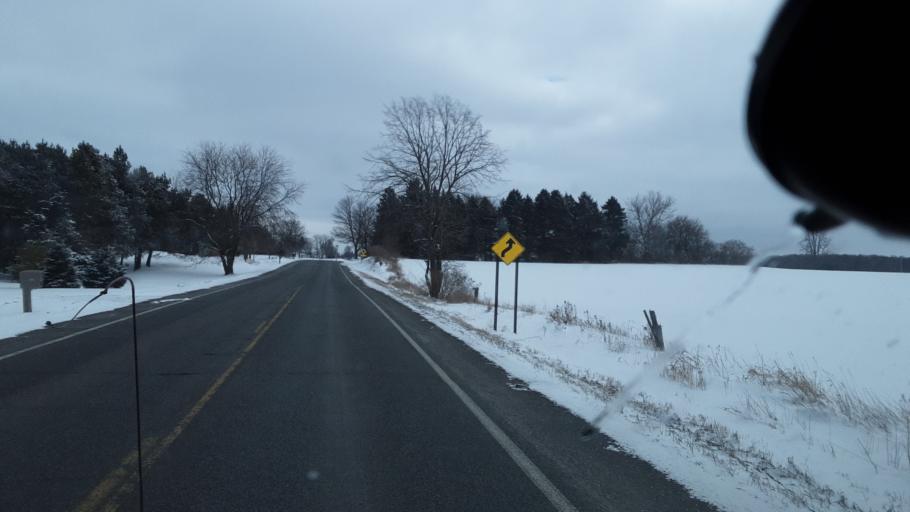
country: US
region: Michigan
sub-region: Ingham County
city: Mason
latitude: 42.5823
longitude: -84.4872
